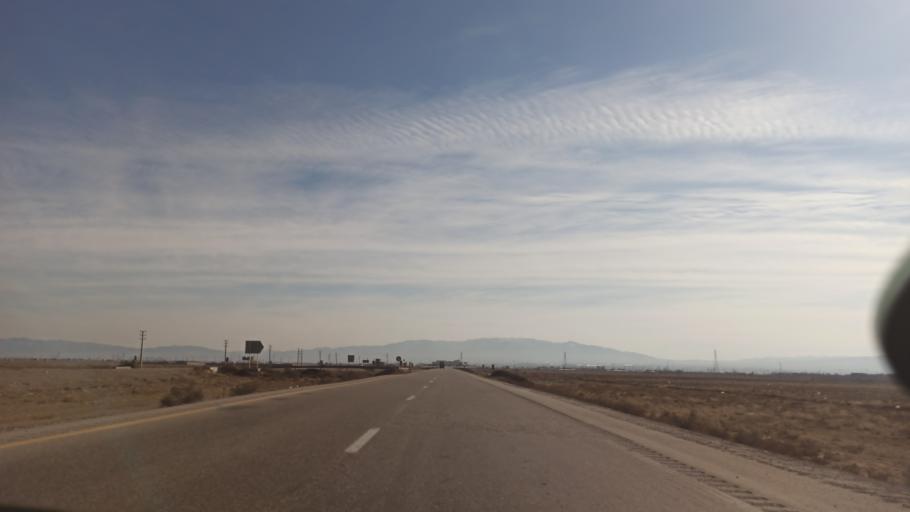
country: IR
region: Qazvin
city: Bu'in Zahra
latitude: 35.7816
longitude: 50.0808
